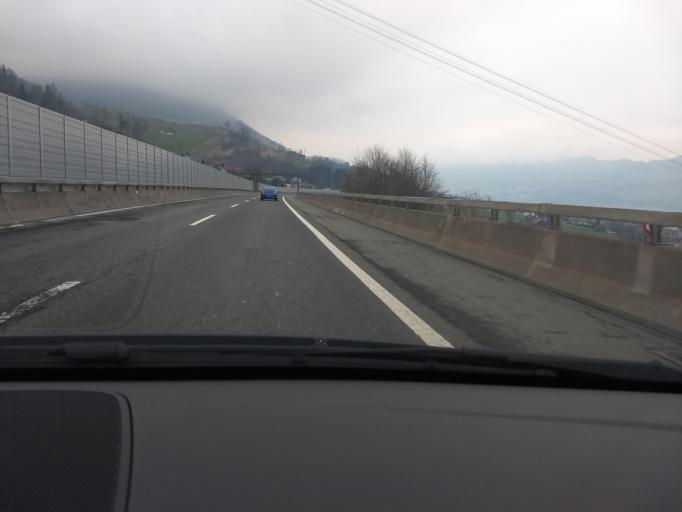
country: CH
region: Nidwalden
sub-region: Nidwalden
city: Beckenried
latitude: 46.9626
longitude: 8.4750
